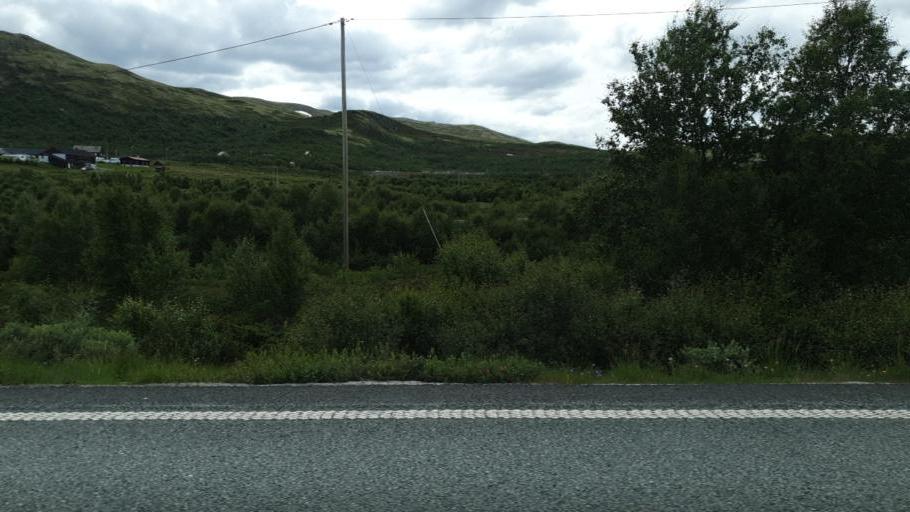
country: NO
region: Oppland
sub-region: Dovre
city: Dovre
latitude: 62.2239
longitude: 9.5501
